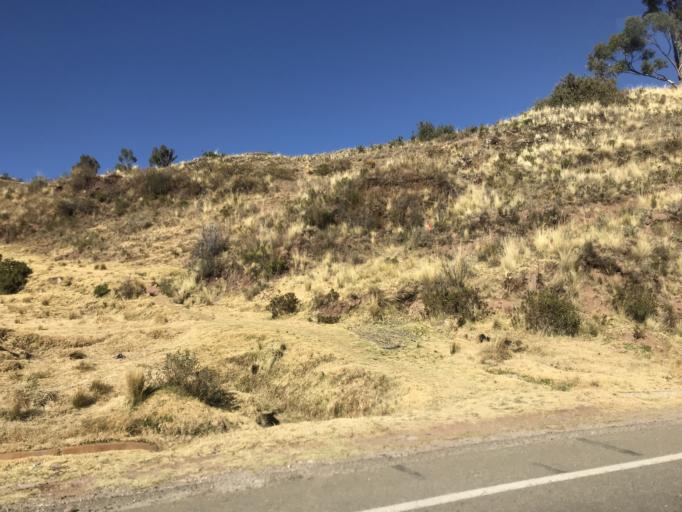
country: PE
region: Puno
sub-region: Yunguyo
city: Yunguyo
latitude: -16.1748
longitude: -69.0648
